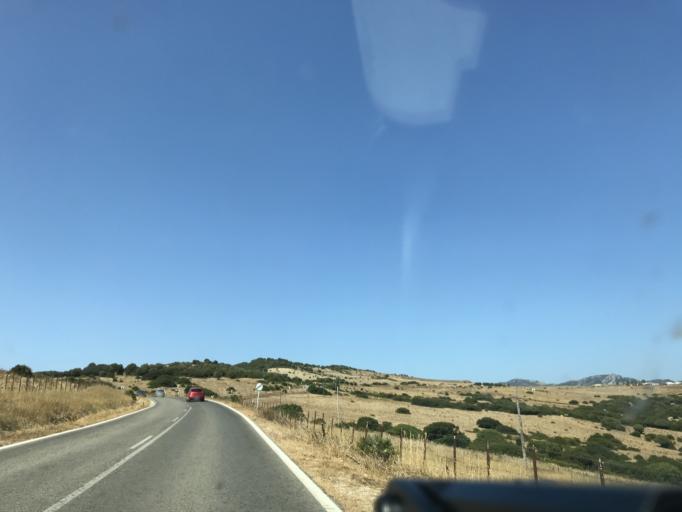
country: ES
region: Andalusia
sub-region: Provincia de Cadiz
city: Zahara de los Atunes
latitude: 36.0990
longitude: -5.7479
